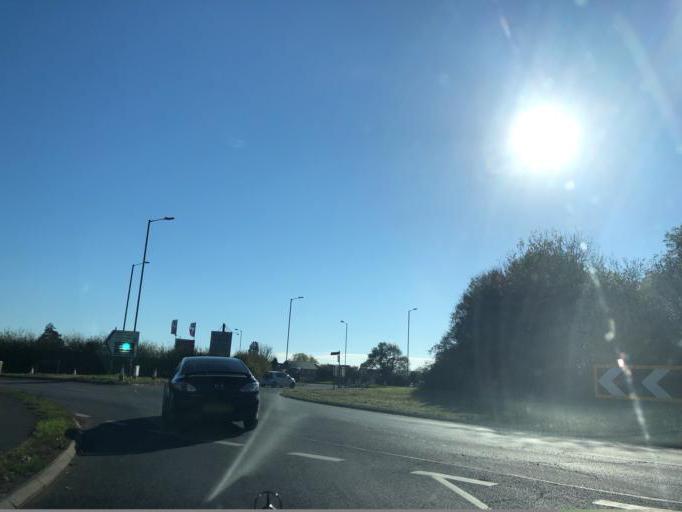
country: GB
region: England
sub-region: Warwickshire
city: Warwick
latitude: 52.2703
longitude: -1.5583
